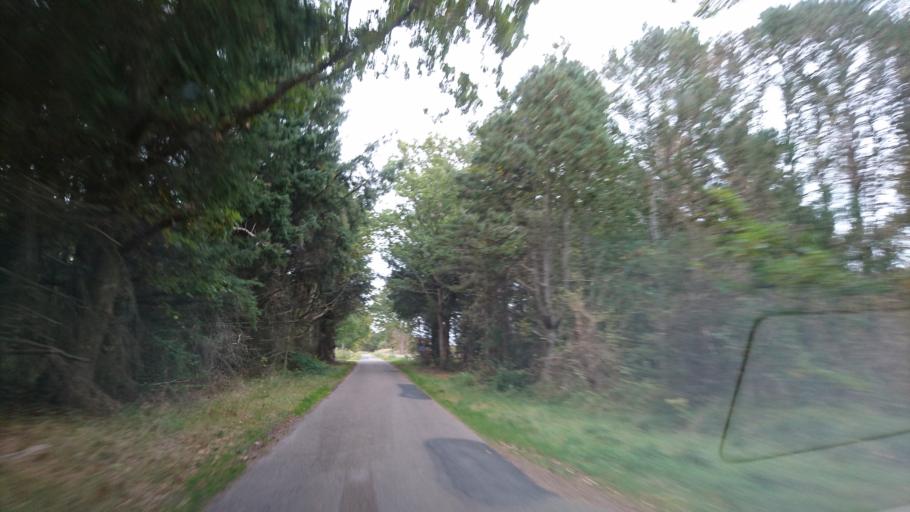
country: DK
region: North Denmark
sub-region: Frederikshavn Kommune
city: Skagen
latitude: 57.6649
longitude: 10.4694
